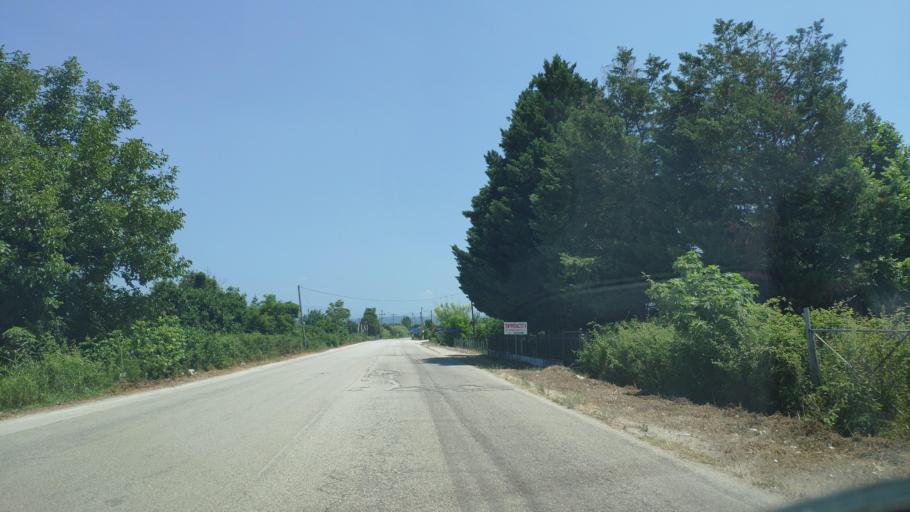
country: GR
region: Epirus
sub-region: Nomos Artas
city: Kostakioi
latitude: 39.1228
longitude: 20.9392
